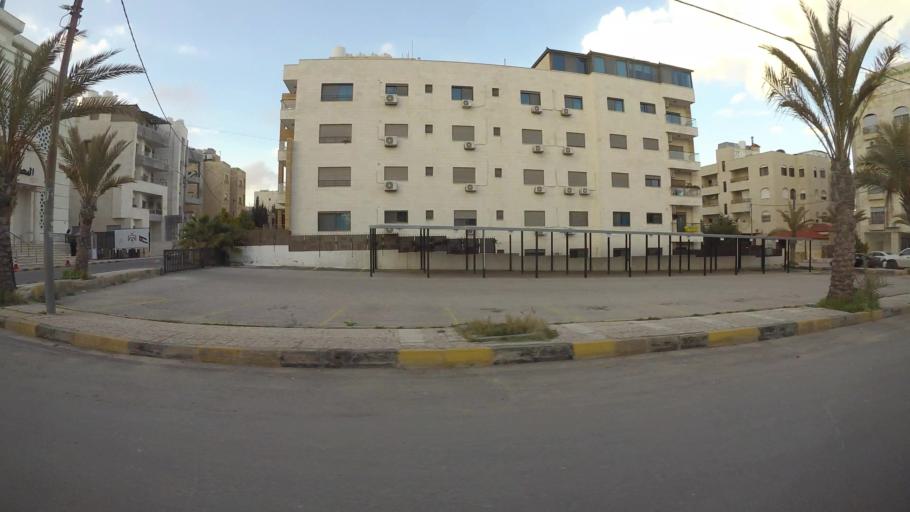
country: JO
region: Amman
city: Al Jubayhah
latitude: 31.9855
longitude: 35.8628
